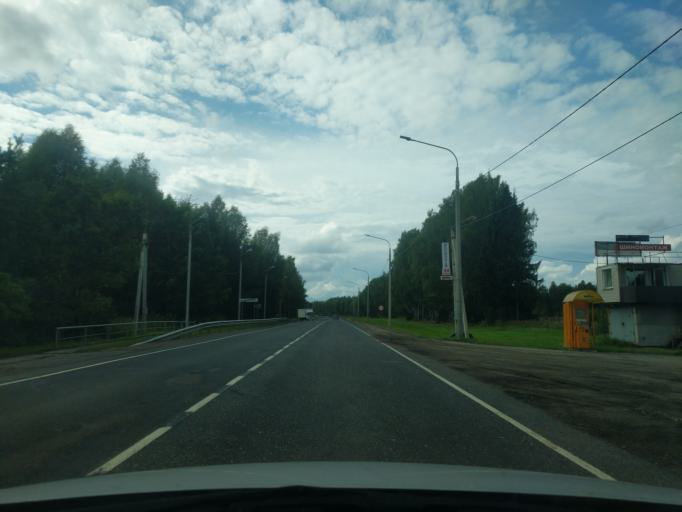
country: RU
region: Jaroslavl
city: Nekrasovskoye
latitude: 57.6361
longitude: 40.4044
